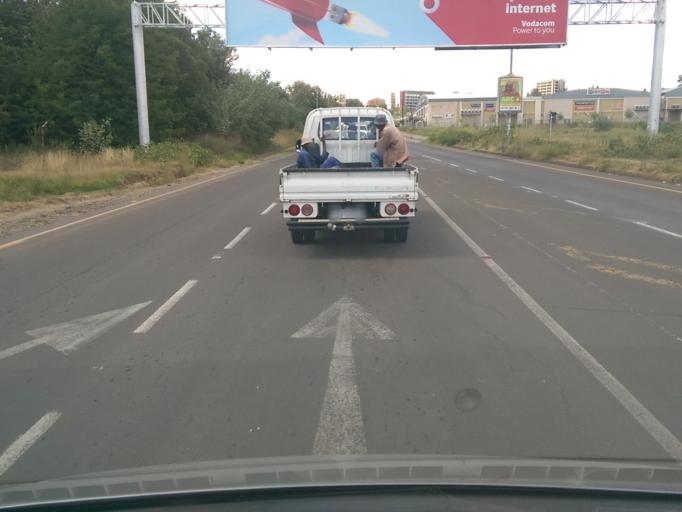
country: LS
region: Maseru
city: Maseru
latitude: -29.3179
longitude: 27.4748
